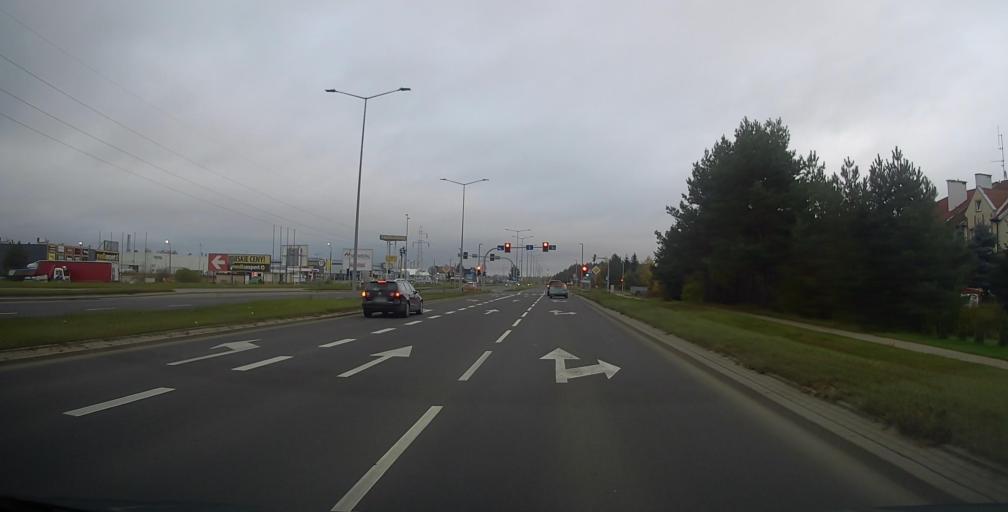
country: PL
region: Warmian-Masurian Voivodeship
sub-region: Powiat elcki
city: Elk
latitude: 53.8105
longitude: 22.3777
